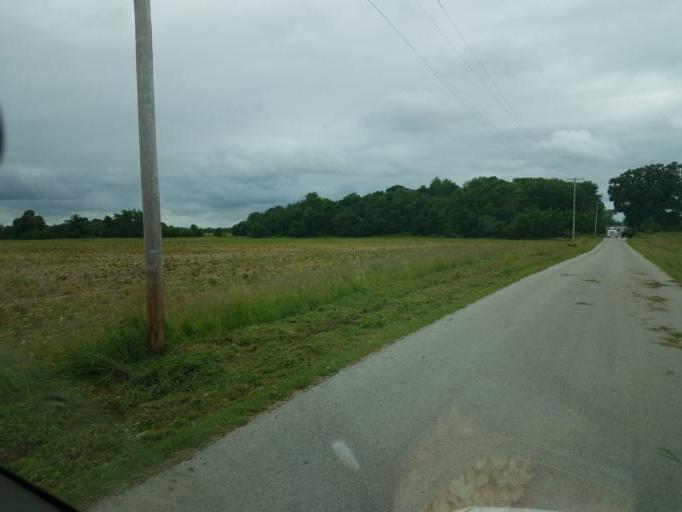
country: US
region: Ohio
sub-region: Morrow County
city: Cardington
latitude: 40.5428
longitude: -82.9017
